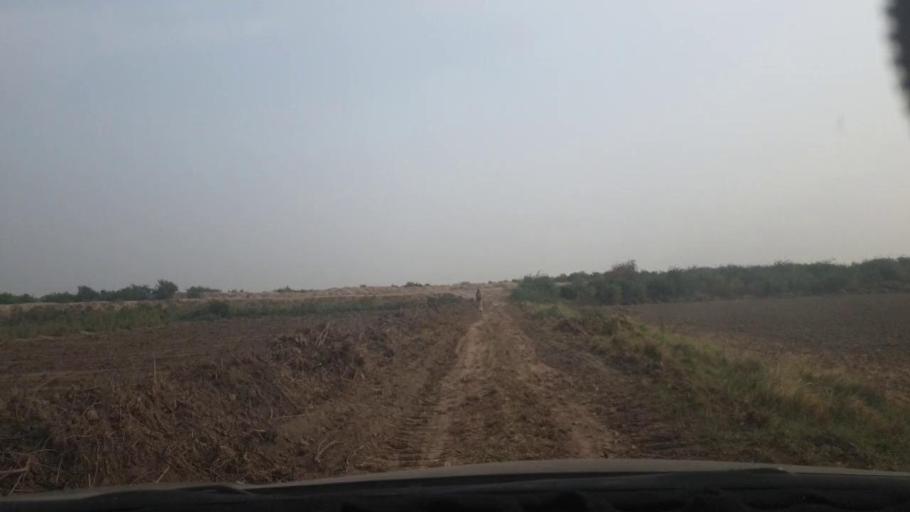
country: PK
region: Sindh
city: Jamshoro
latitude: 25.5185
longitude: 68.3224
